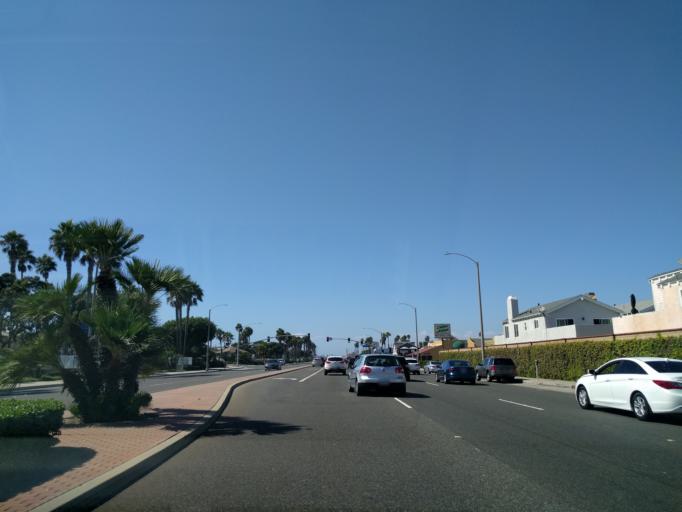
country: US
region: California
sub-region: Orange County
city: Newport Beach
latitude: 33.6276
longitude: -117.9512
